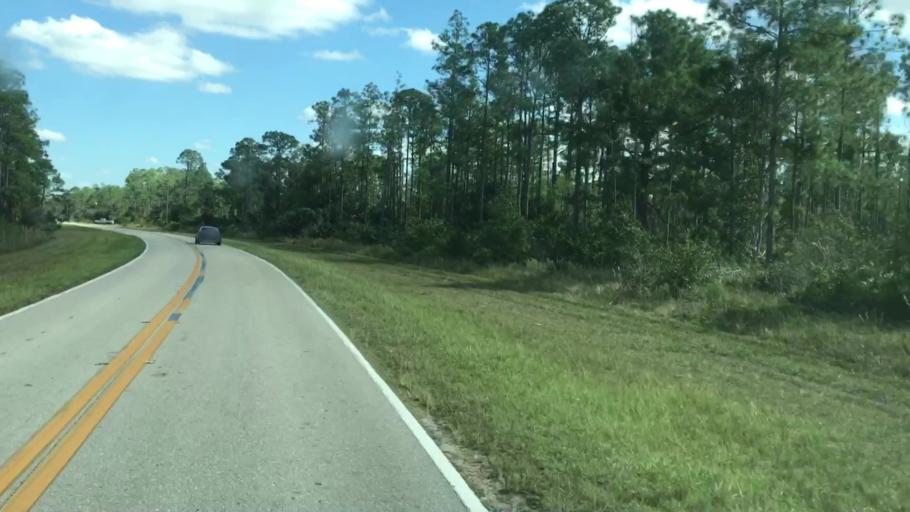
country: US
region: Florida
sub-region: Lee County
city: Alva
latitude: 26.6775
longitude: -81.6223
